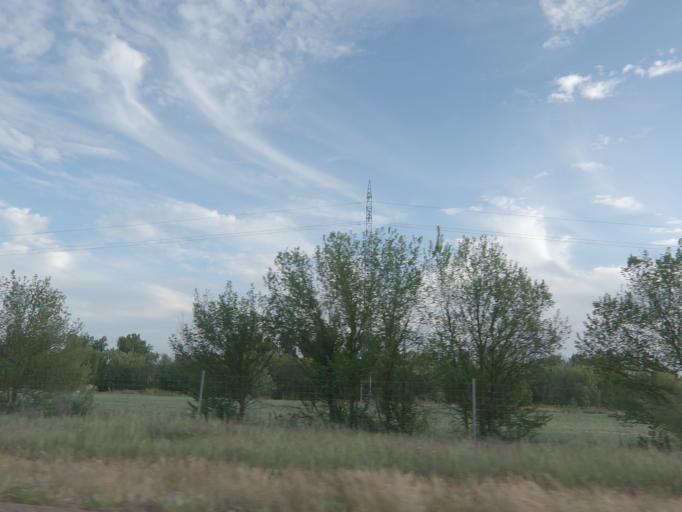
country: ES
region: Extremadura
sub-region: Provincia de Badajoz
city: Lobon
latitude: 38.8412
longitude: -6.6680
